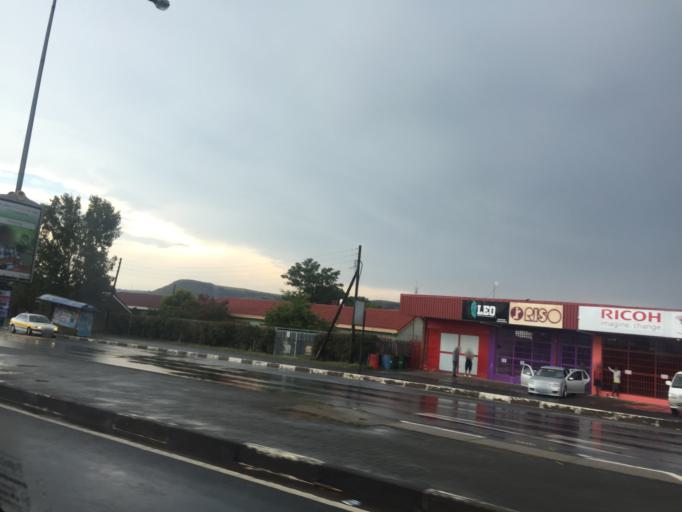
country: LS
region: Maseru
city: Maseru
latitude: -29.3039
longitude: 27.4662
